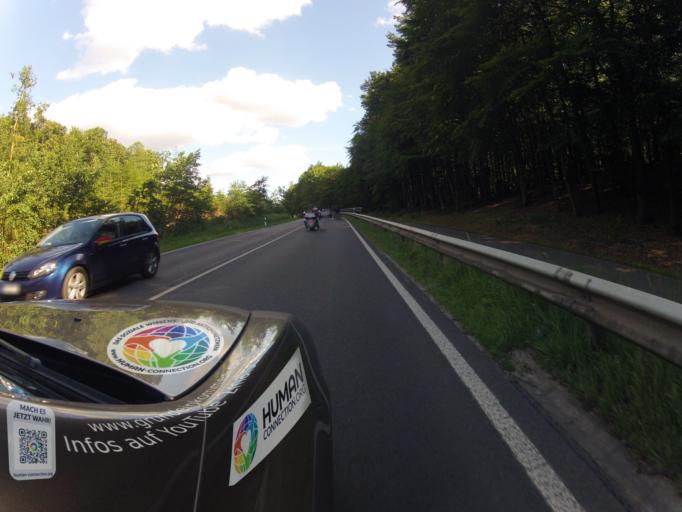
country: DE
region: Mecklenburg-Vorpommern
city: Seebad Bansin
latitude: 53.9704
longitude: 14.1184
